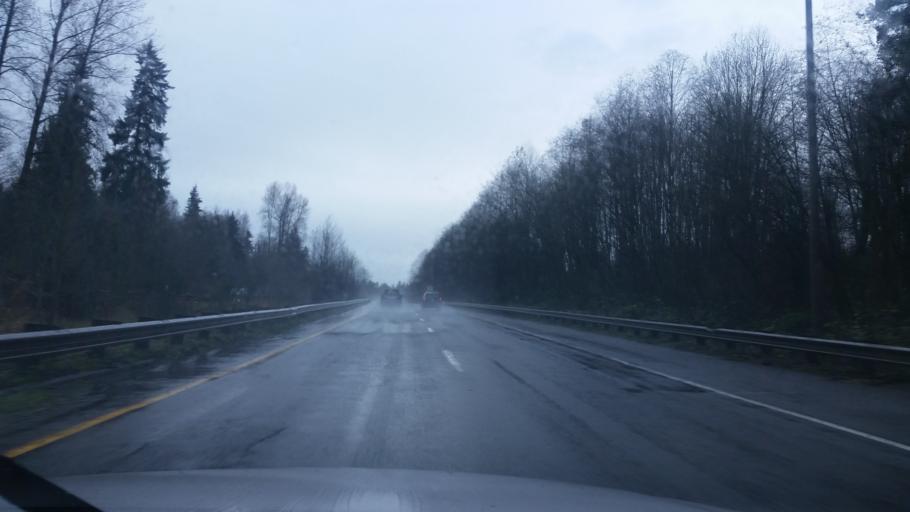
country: US
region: Washington
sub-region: King County
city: Hobart
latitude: 47.4296
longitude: -121.9880
